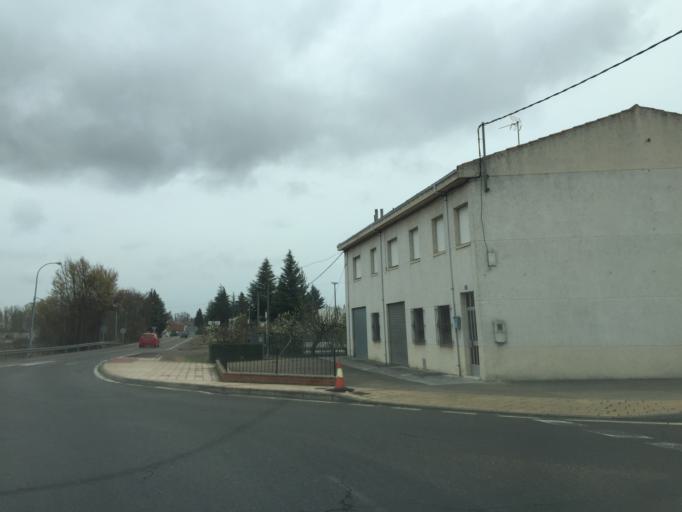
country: ES
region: Castille and Leon
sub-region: Provincia de Leon
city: San Andres del Rabanedo
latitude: 42.6364
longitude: -5.6114
